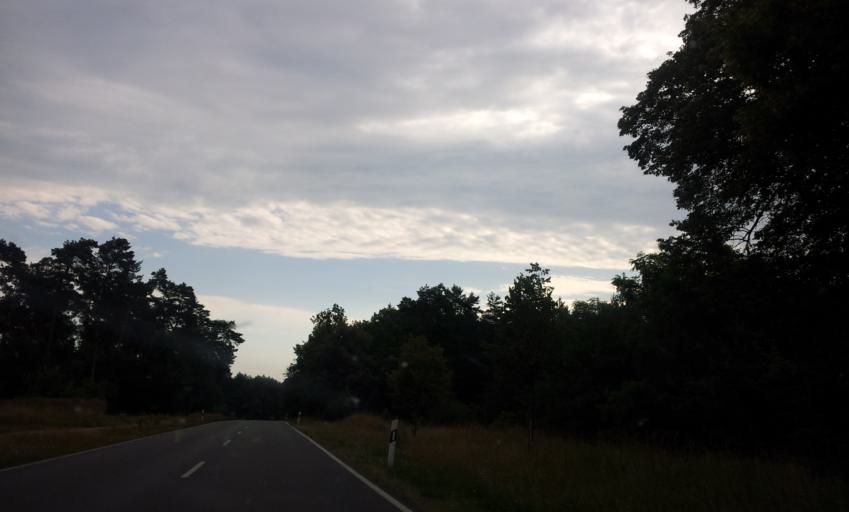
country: DE
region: Brandenburg
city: Juterbog
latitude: 52.0085
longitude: 13.0650
